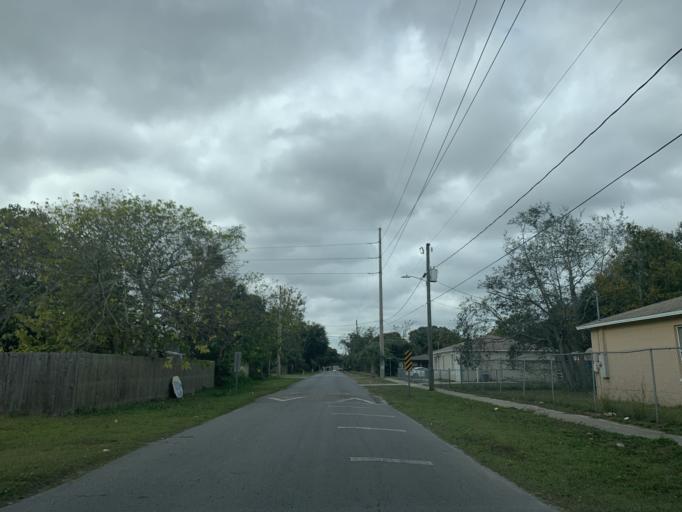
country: US
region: Florida
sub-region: Hillsborough County
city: East Lake-Orient Park
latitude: 27.9778
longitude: -82.3969
